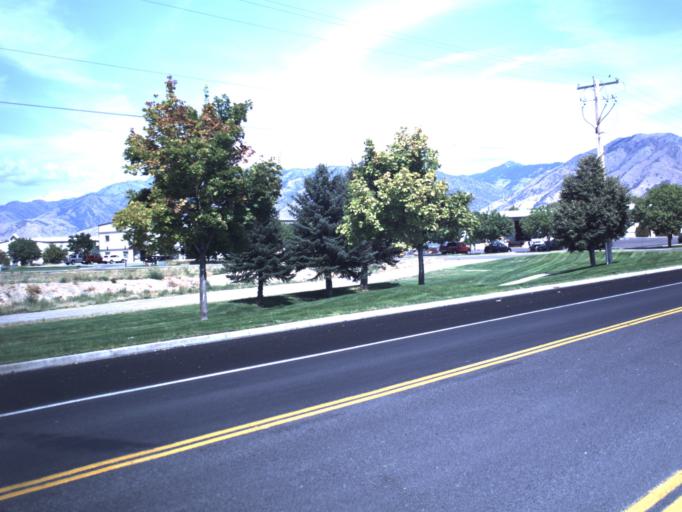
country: US
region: Utah
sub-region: Cache County
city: Logan
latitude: 41.7356
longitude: -111.8570
